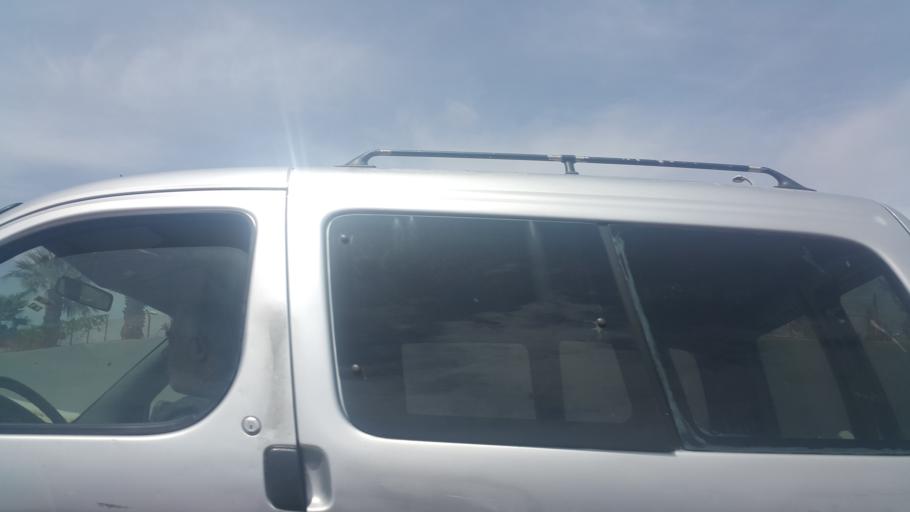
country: TR
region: Adana
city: Yakapinar
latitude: 36.9655
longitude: 35.6220
